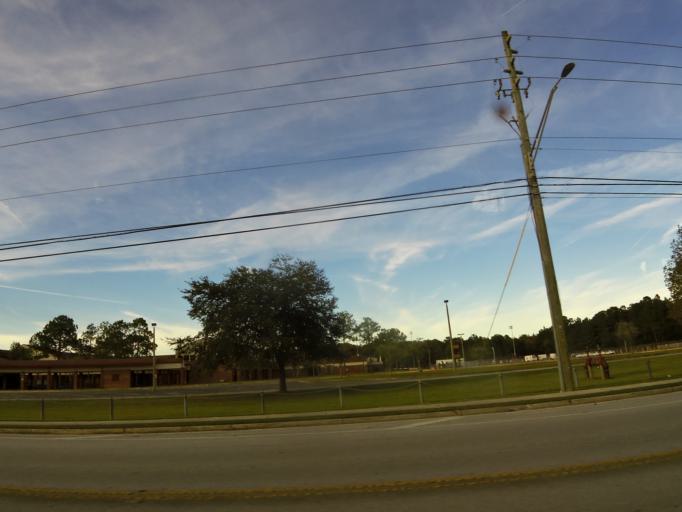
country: US
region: Florida
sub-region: Saint Johns County
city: Fruit Cove
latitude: 30.1613
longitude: -81.5832
